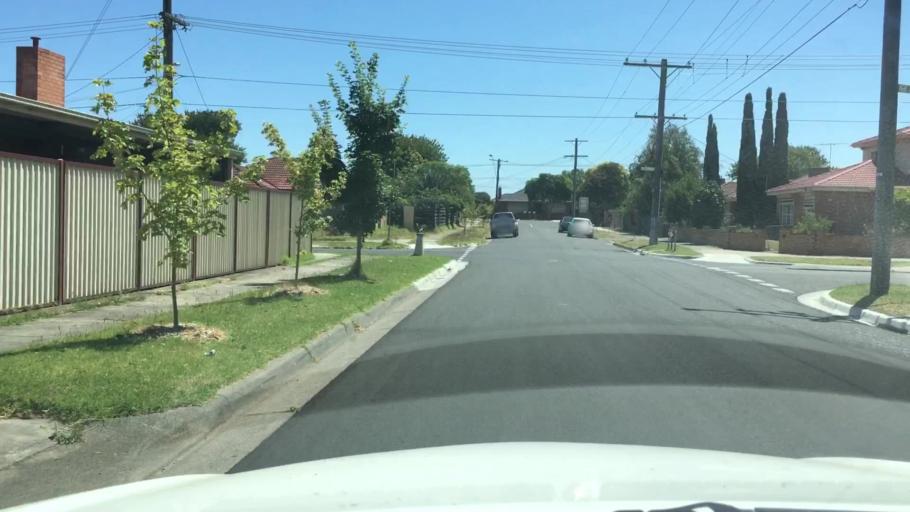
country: AU
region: Victoria
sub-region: Greater Dandenong
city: Springvale South
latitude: -37.9563
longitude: 145.1428
